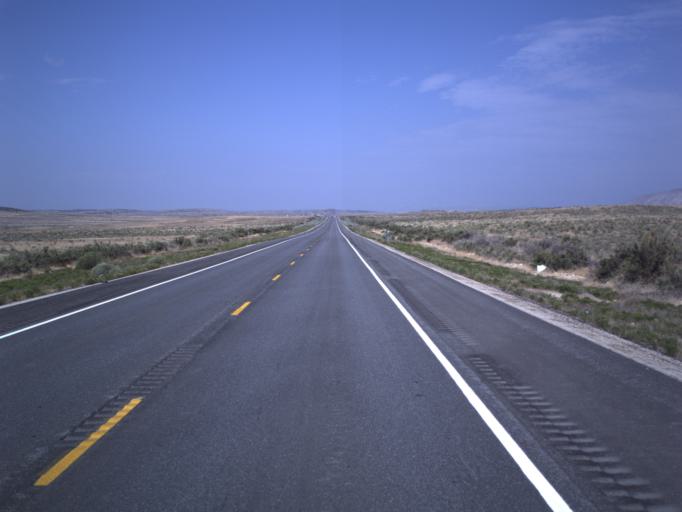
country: US
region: Colorado
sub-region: Rio Blanco County
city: Rangely
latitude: 40.2814
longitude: -109.0819
